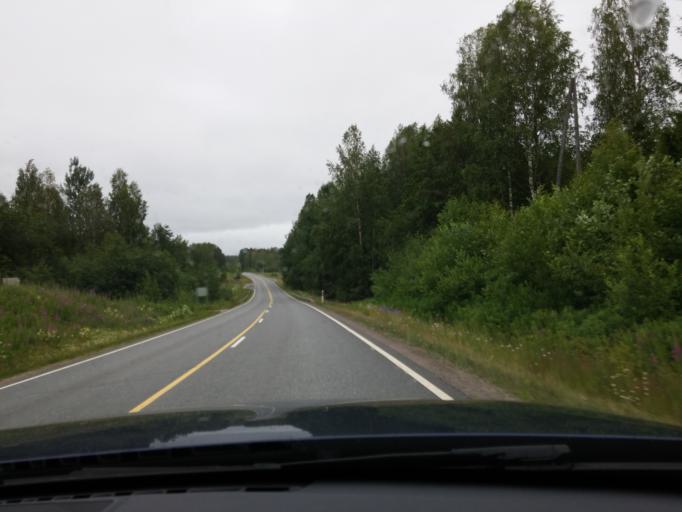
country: FI
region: Central Finland
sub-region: Joutsa
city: Joutsa
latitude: 61.7864
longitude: 26.0376
